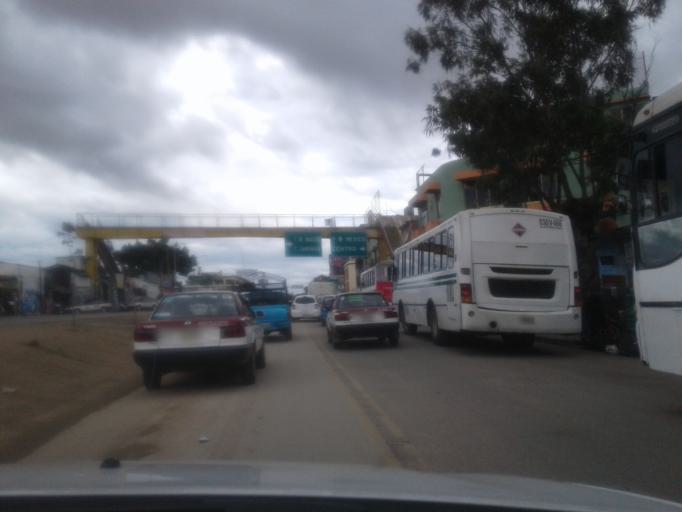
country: MX
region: Oaxaca
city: Oaxaca de Juarez
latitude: 17.0598
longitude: -96.7329
